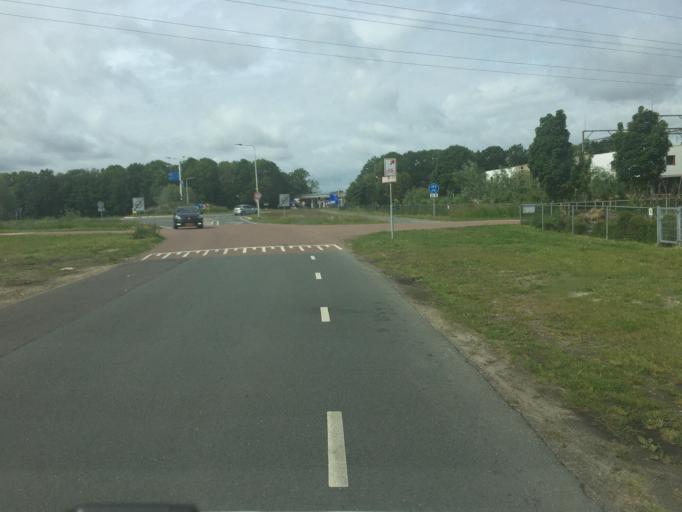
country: NL
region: Friesland
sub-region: Gemeente Lemsterland
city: Lemmer
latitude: 52.8483
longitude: 5.7258
